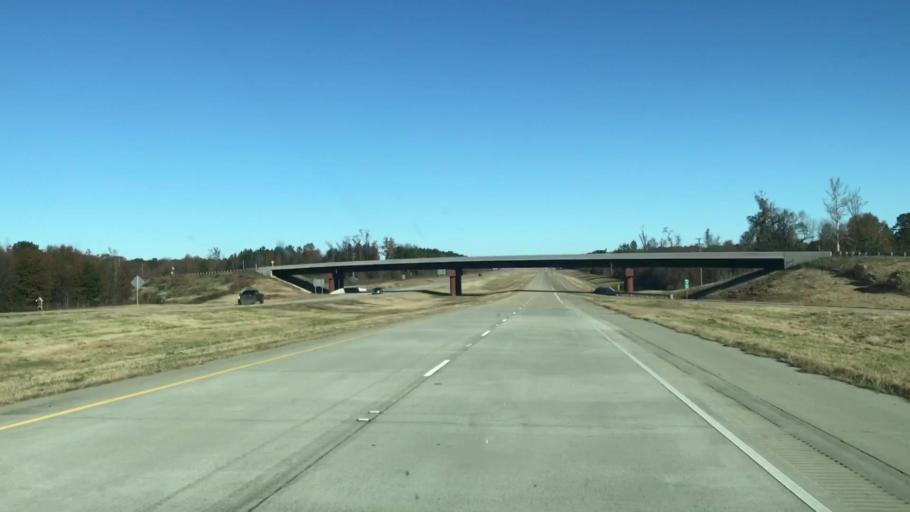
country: US
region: Louisiana
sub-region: Caddo Parish
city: Blanchard
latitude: 32.5987
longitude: -93.8320
